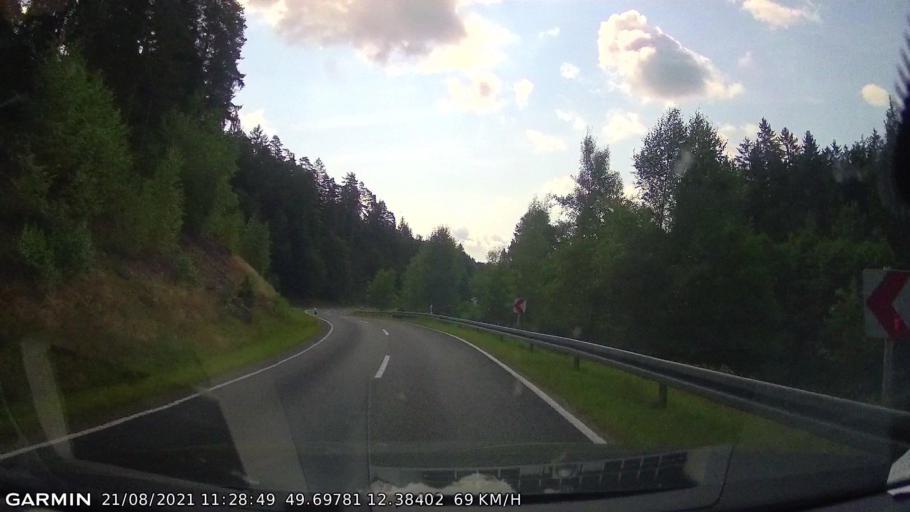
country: DE
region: Bavaria
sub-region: Upper Palatinate
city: Georgenberg
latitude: 49.6976
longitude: 12.3839
